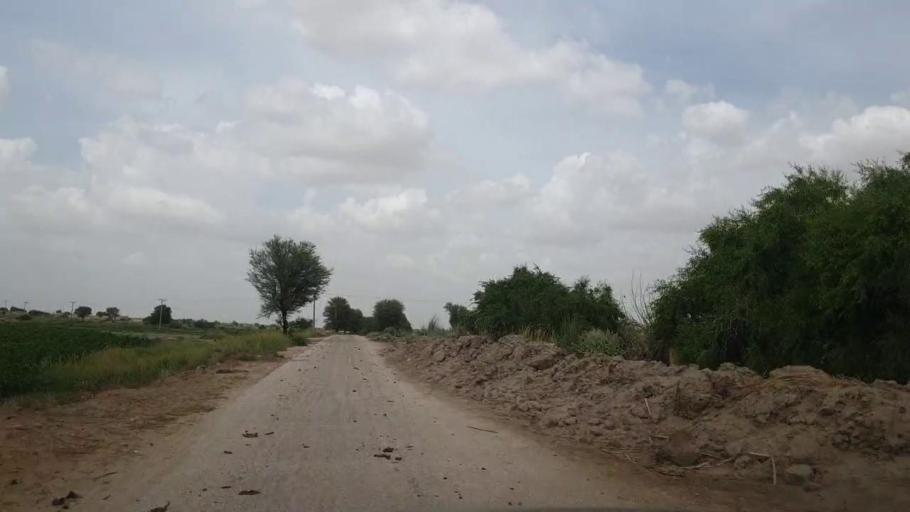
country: PK
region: Sindh
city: Kot Diji
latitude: 27.2239
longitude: 69.0857
